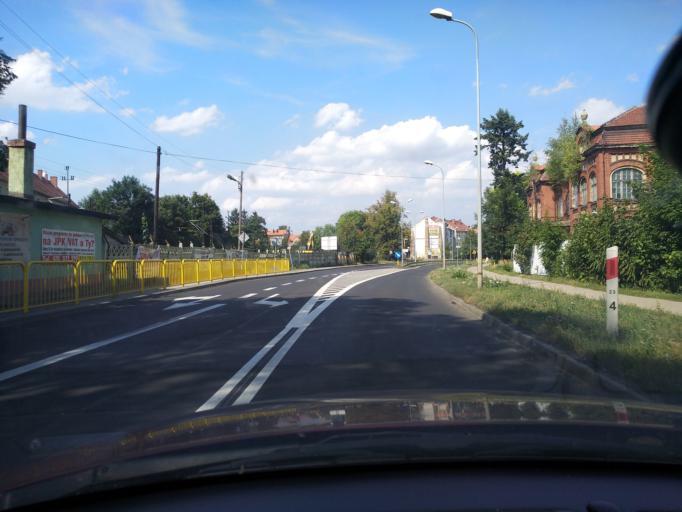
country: PL
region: Lower Silesian Voivodeship
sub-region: Powiat lubanski
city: Luban
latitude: 51.1147
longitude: 15.2934
